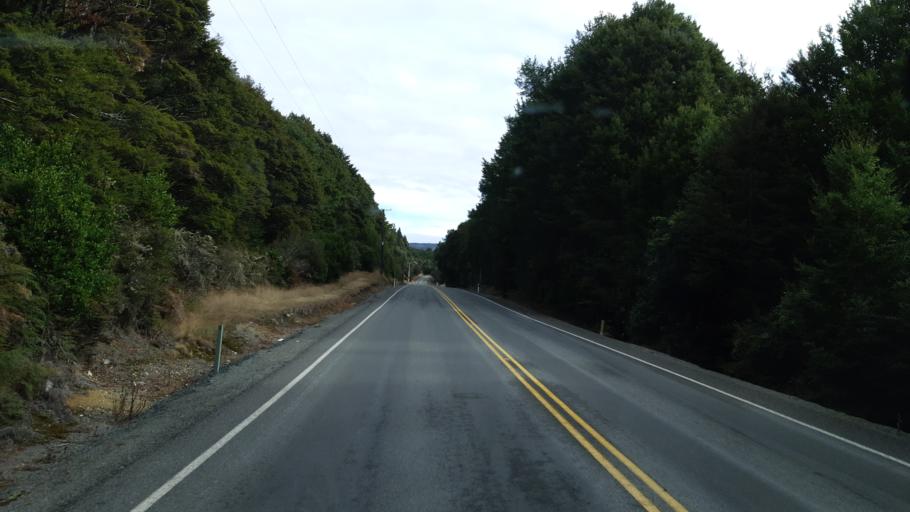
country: NZ
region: Tasman
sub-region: Tasman District
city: Wakefield
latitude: -41.7765
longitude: 172.9240
